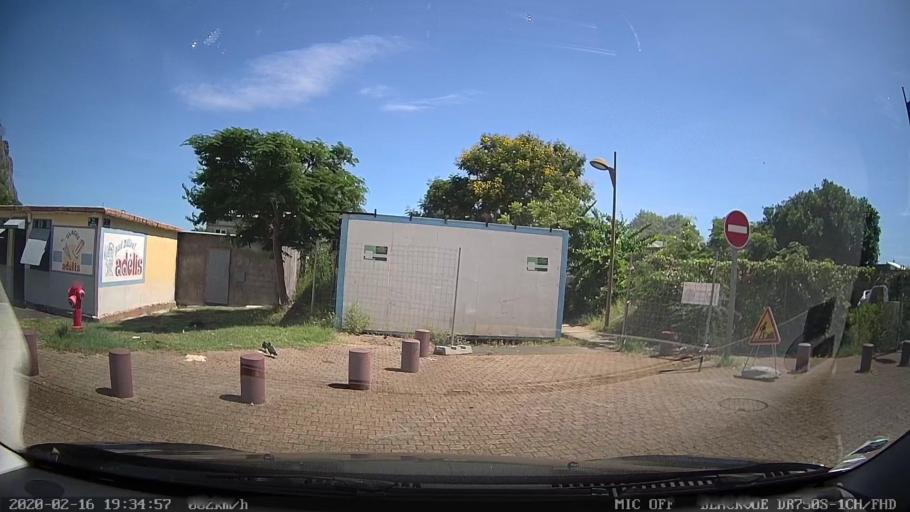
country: RE
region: Reunion
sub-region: Reunion
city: Saint-Denis
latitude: -20.8802
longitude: 55.4409
